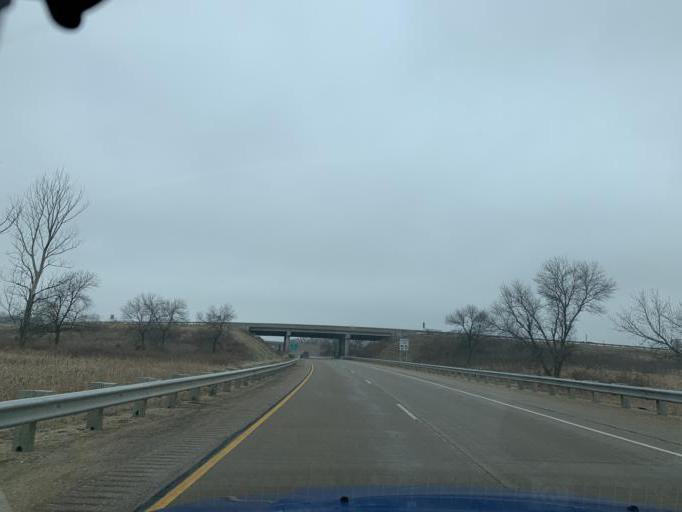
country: US
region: Wisconsin
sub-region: Dane County
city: McFarland
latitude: 43.0466
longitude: -89.2715
